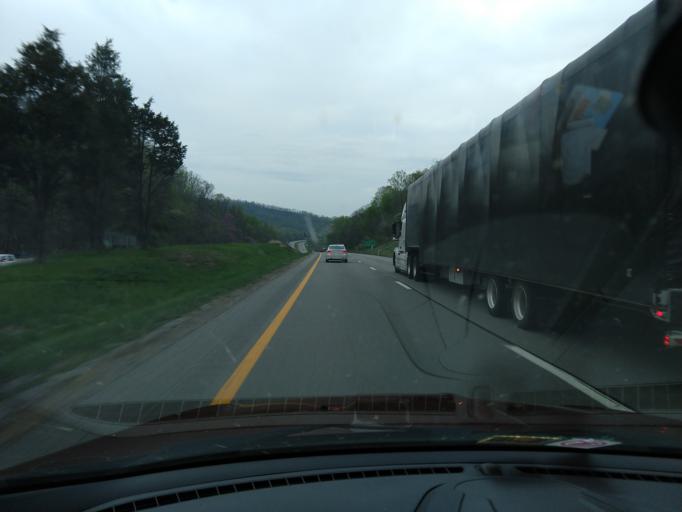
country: US
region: West Virginia
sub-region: Lewis County
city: Weston
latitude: 39.1162
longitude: -80.3884
